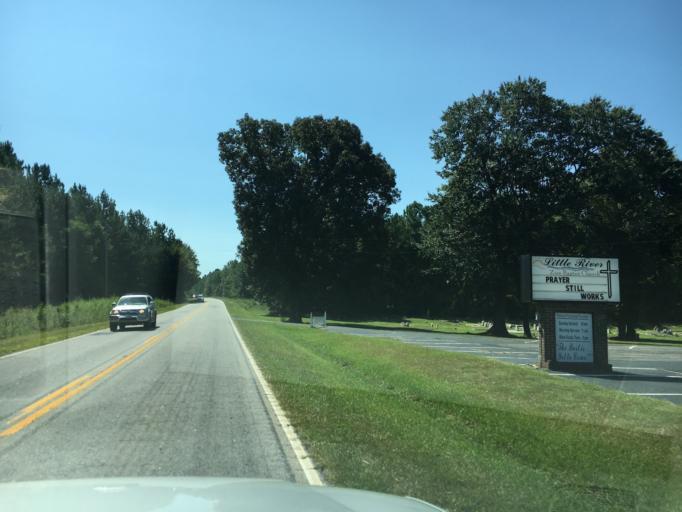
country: US
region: South Carolina
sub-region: Laurens County
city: Joanna
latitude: 34.3378
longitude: -81.8540
